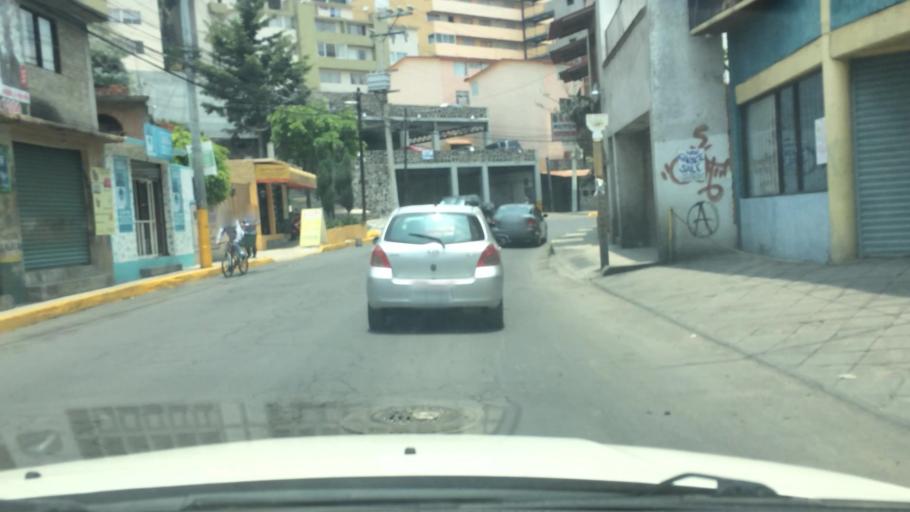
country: MX
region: Mexico City
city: Tlalpan
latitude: 19.2725
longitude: -99.1605
